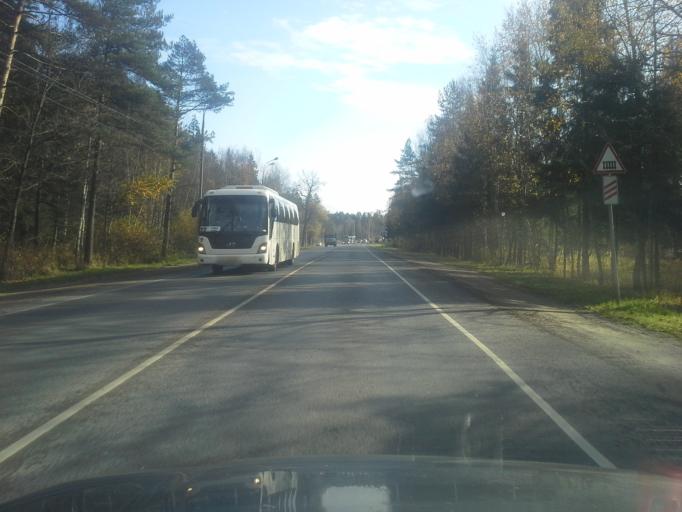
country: RU
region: Moskovskaya
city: Bol'shiye Vyazemy
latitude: 55.6727
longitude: 36.9435
